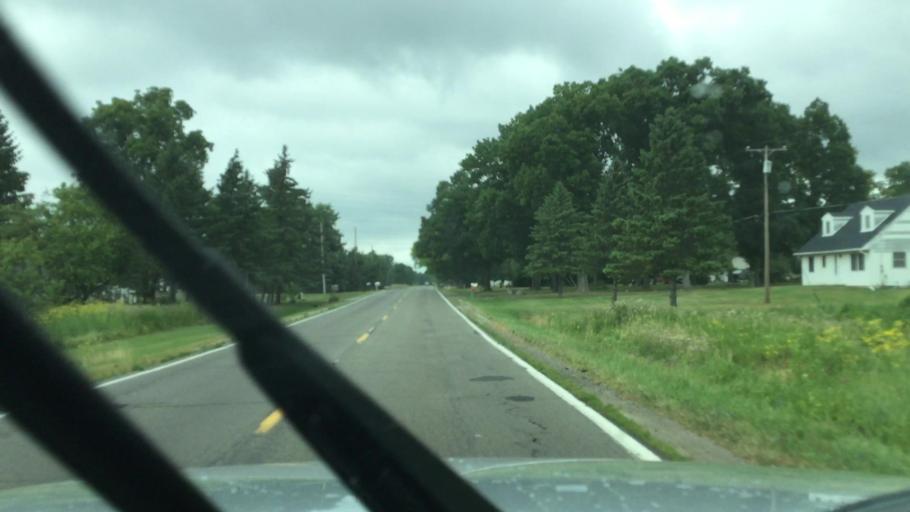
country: US
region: Michigan
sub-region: Genesee County
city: Clio
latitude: 43.1253
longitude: -83.7738
